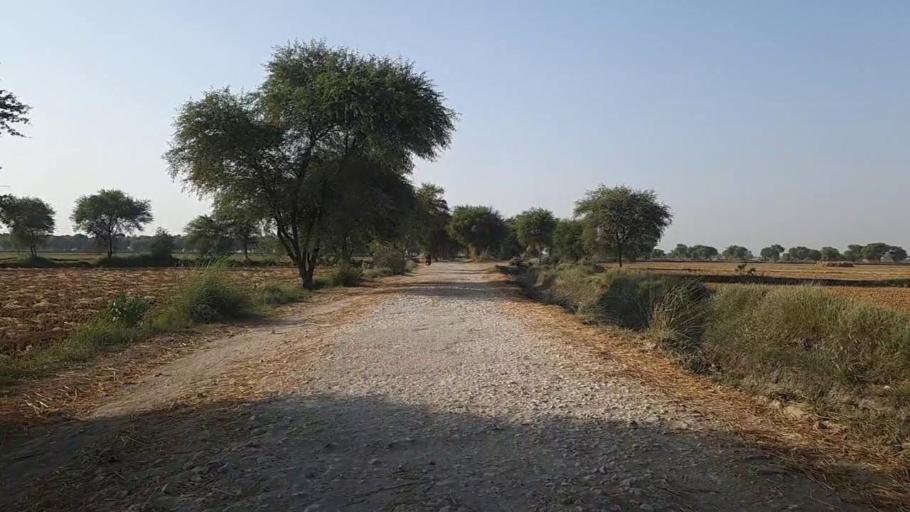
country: PK
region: Sindh
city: Kashmor
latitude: 28.4047
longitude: 69.4157
